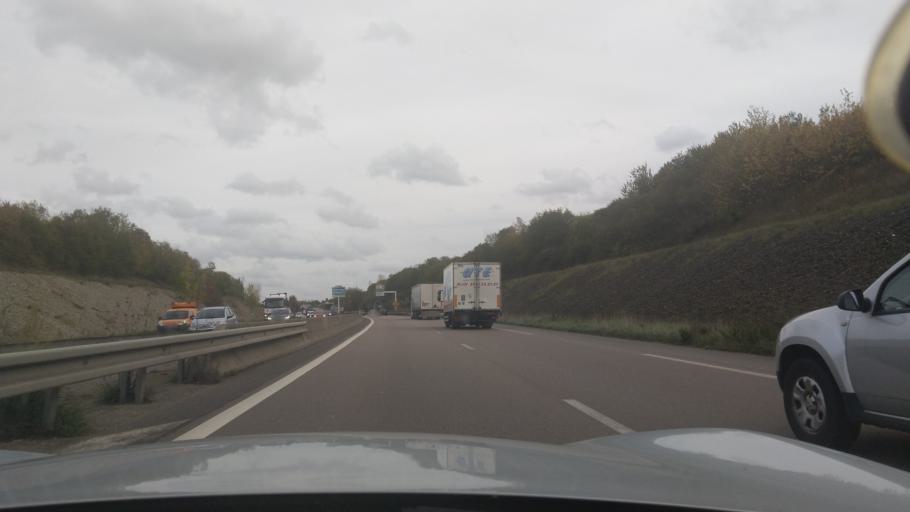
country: FR
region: Ile-de-France
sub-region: Departement du Val-d'Oise
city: Louvres
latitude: 49.0326
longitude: 2.4909
